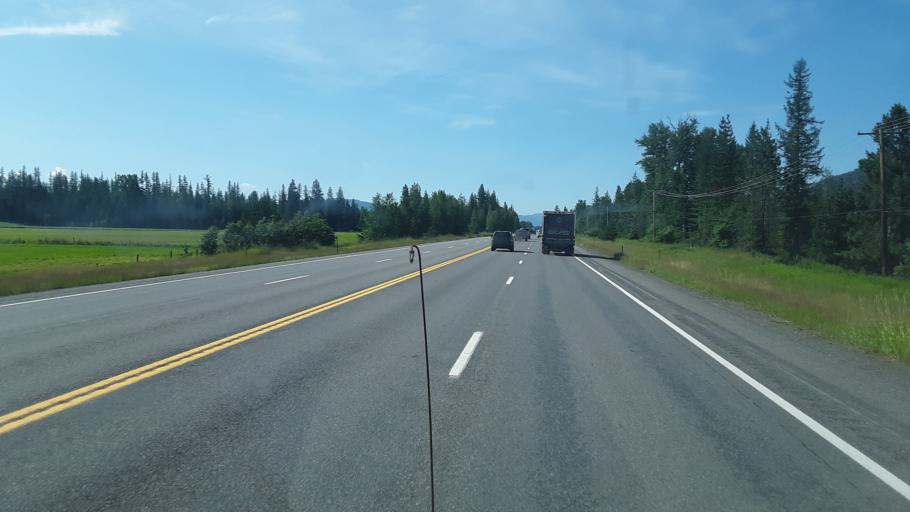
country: US
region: Idaho
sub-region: Bonner County
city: Ponderay
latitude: 48.3689
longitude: -116.5473
